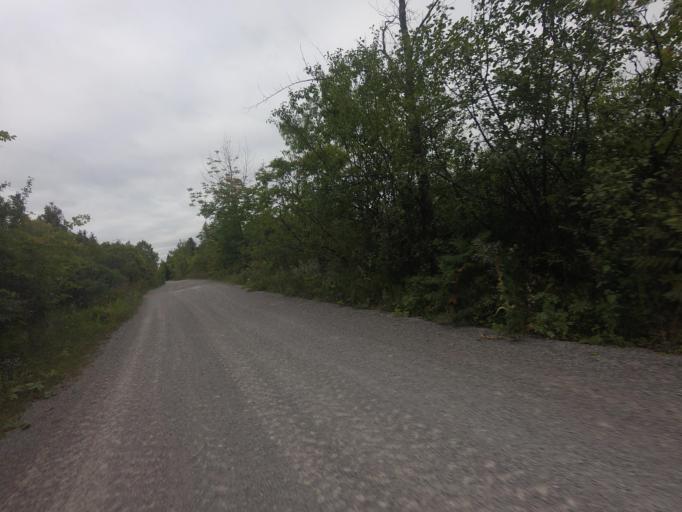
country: CA
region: Ontario
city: Omemee
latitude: 44.5200
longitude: -78.7330
